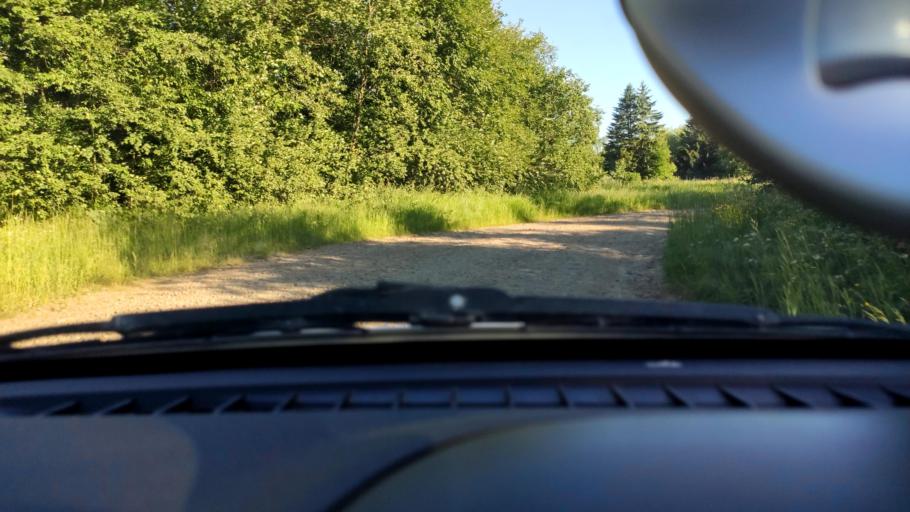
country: RU
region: Perm
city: Bershet'
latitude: 57.6947
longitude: 56.4022
